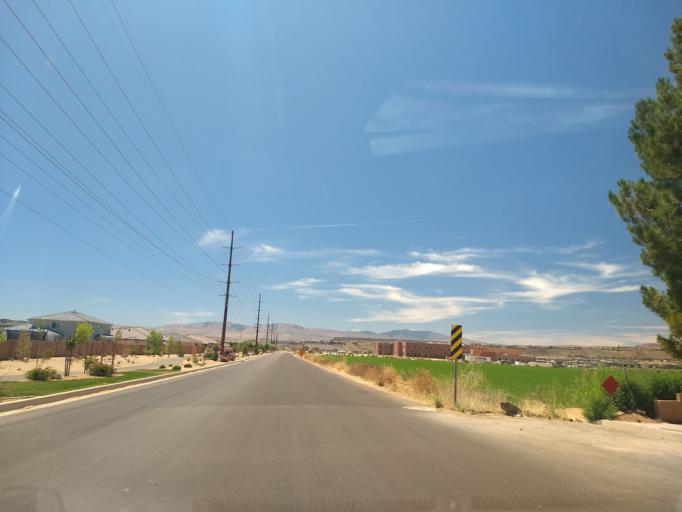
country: US
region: Utah
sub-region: Washington County
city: Washington
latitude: 37.0888
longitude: -113.5102
